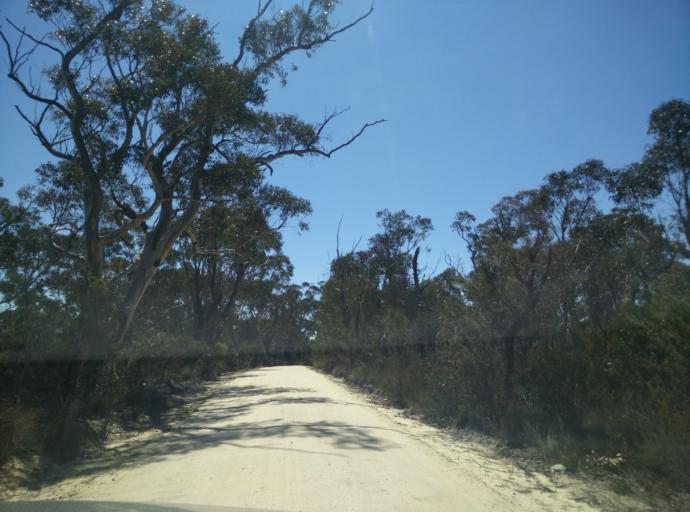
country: AU
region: New South Wales
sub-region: Blue Mountains Municipality
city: Blackheath
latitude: -33.5699
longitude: 150.2788
